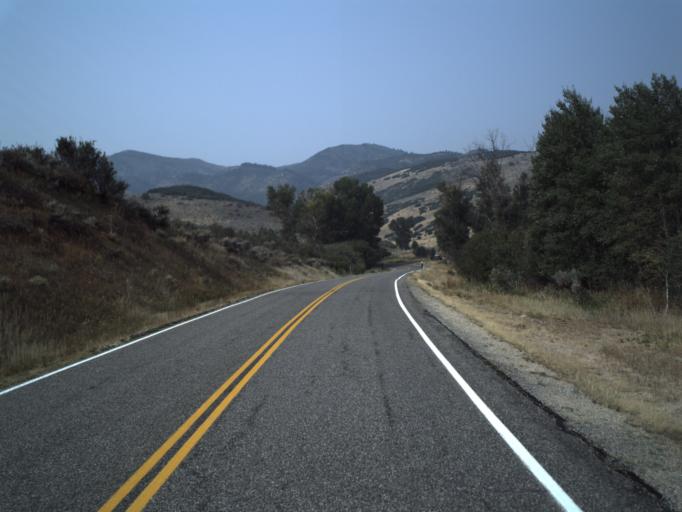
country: US
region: Utah
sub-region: Summit County
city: Coalville
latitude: 40.9860
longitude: -111.5331
